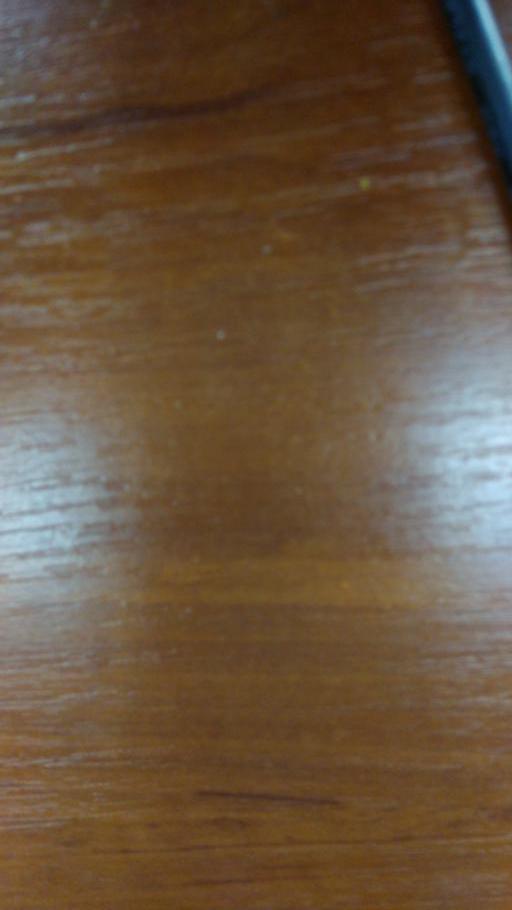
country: RU
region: Tverskaya
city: Emmaus
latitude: 56.7839
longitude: 36.0815
